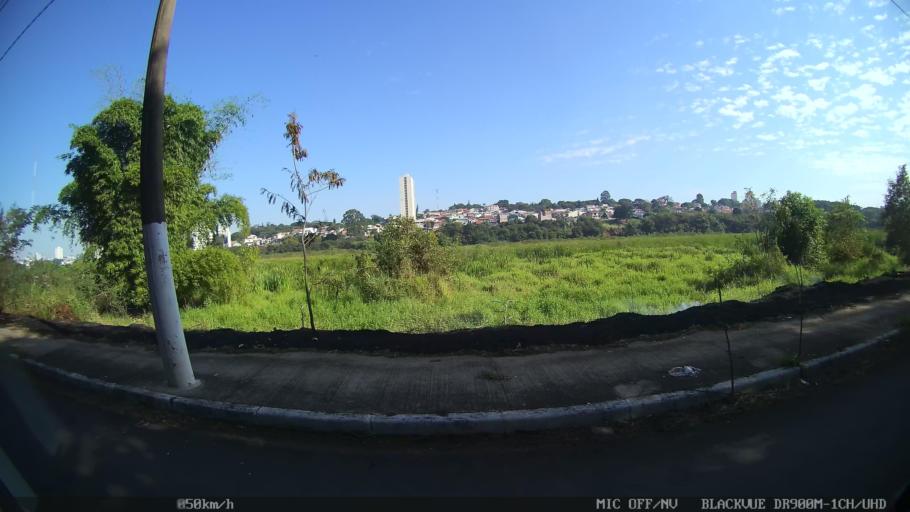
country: BR
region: Sao Paulo
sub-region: Americana
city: Americana
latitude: -22.7302
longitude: -47.3294
